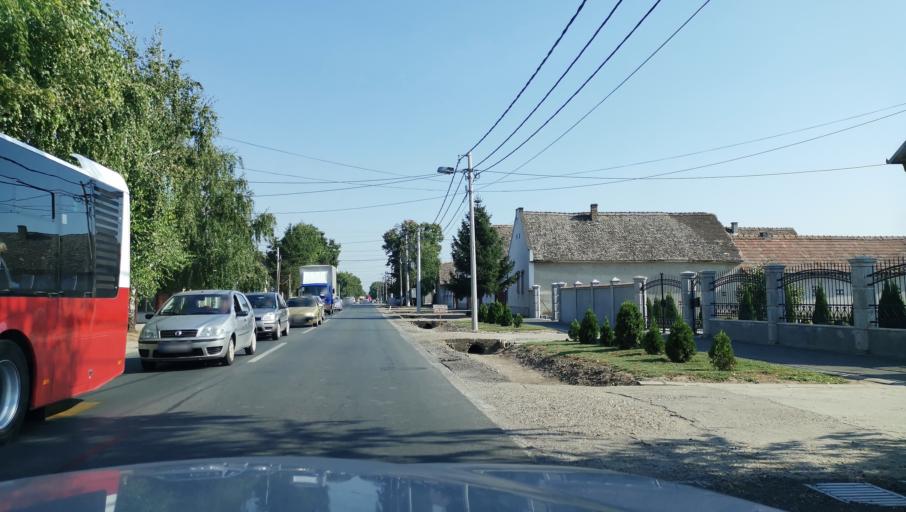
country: RS
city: Dobanovci
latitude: 44.8321
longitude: 20.2194
